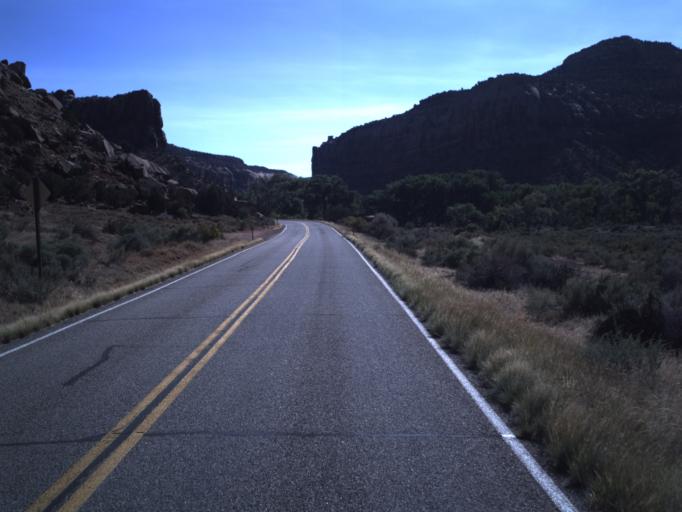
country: US
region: Utah
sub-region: San Juan County
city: Monticello
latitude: 38.0425
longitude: -109.5524
